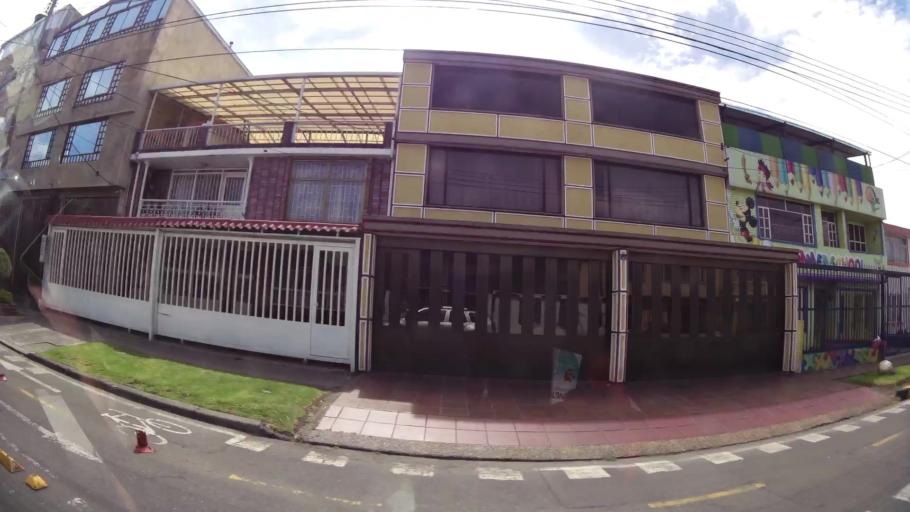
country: CO
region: Bogota D.C.
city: Bogota
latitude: 4.6285
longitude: -74.1335
